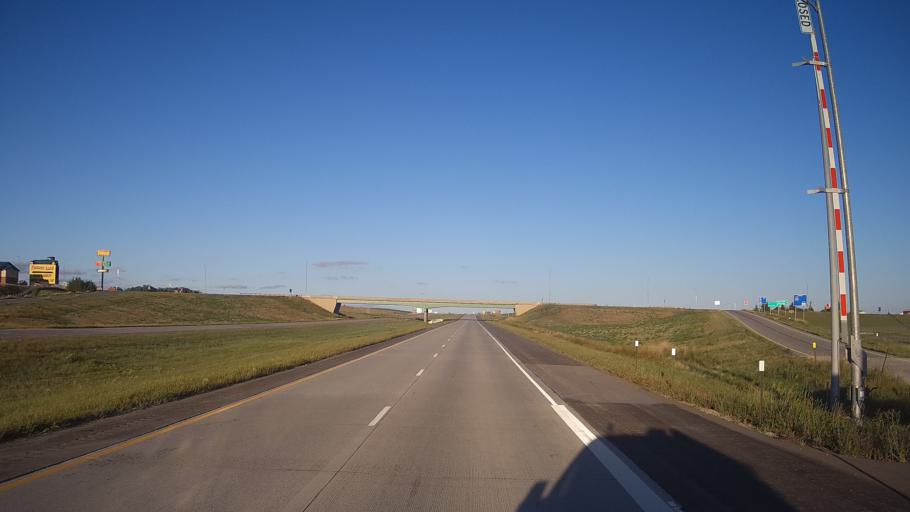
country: US
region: South Dakota
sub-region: Jones County
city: Murdo
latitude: 43.8830
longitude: -100.7097
